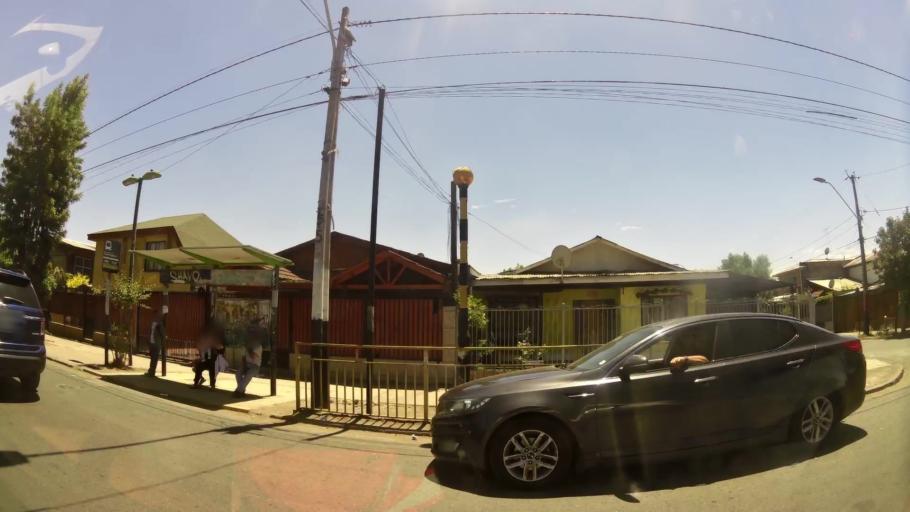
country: CL
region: Santiago Metropolitan
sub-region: Provincia de Santiago
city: La Pintana
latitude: -33.5560
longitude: -70.6475
